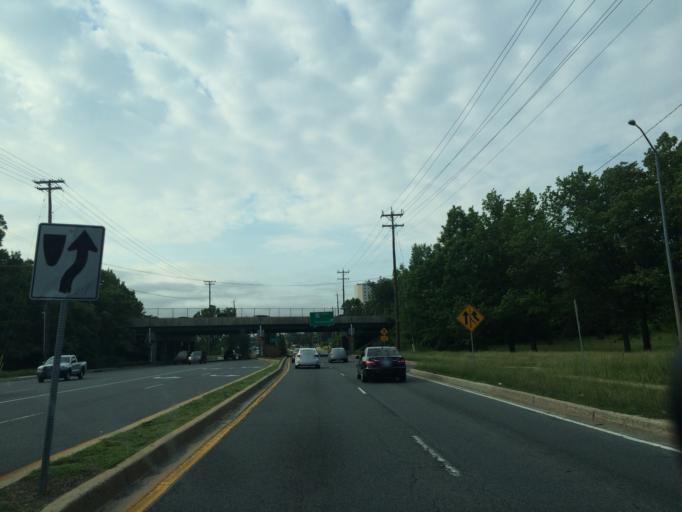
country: US
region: Maryland
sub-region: Montgomery County
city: White Oak
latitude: 39.0445
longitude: -76.9922
